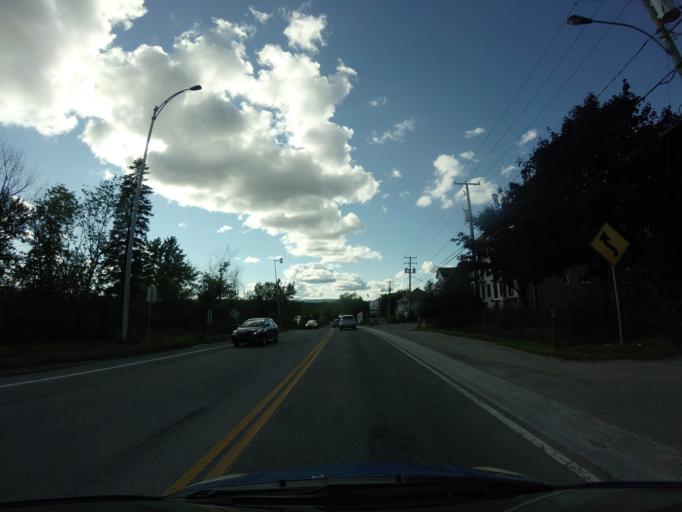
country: CA
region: Quebec
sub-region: Outaouais
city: Gatineau
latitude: 45.4757
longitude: -75.7317
